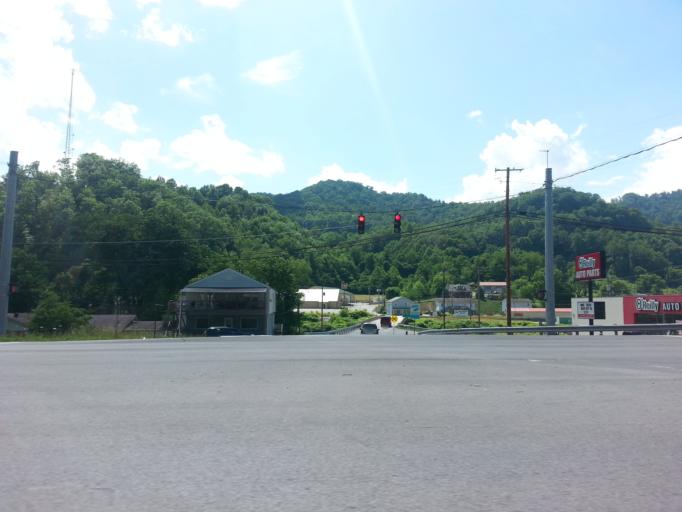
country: US
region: Kentucky
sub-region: Harlan County
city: Harlan
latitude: 36.8321
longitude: -83.3248
